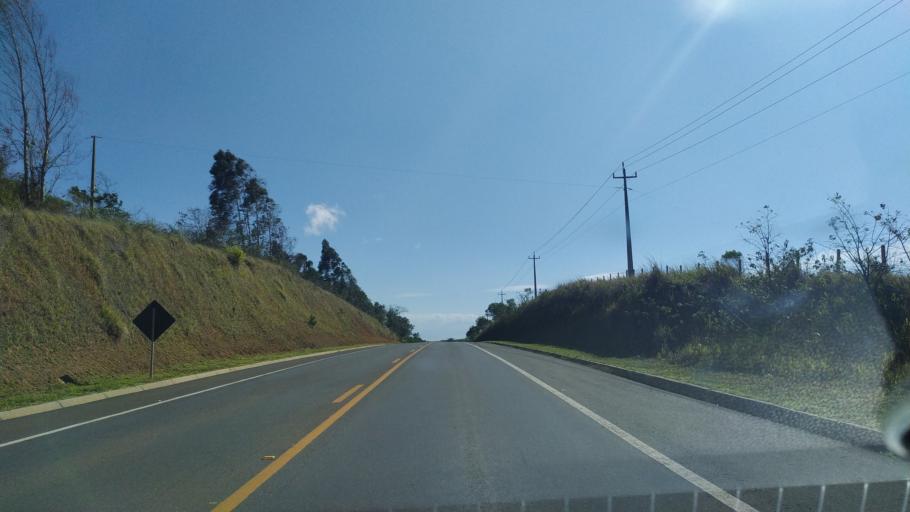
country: BR
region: Parana
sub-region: Ortigueira
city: Ortigueira
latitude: -24.2952
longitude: -50.8246
